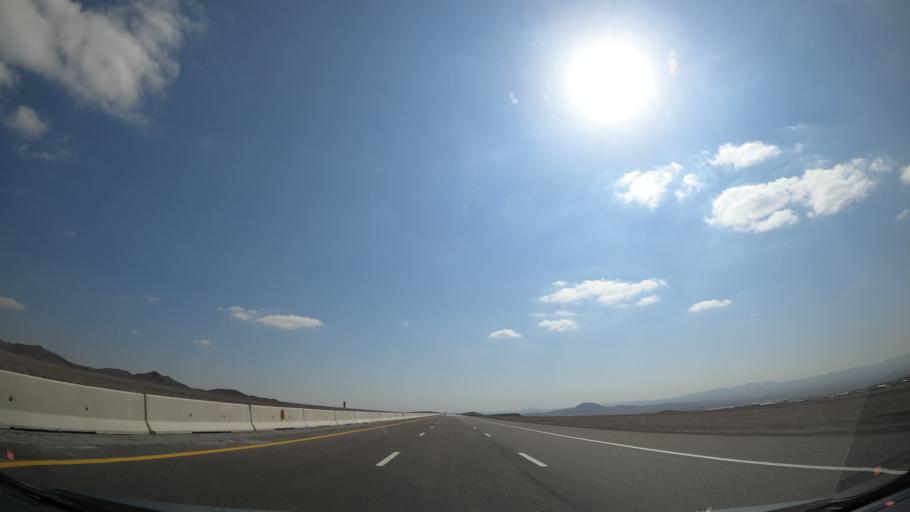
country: IR
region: Alborz
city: Nazarabad
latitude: 35.6745
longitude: 50.6448
